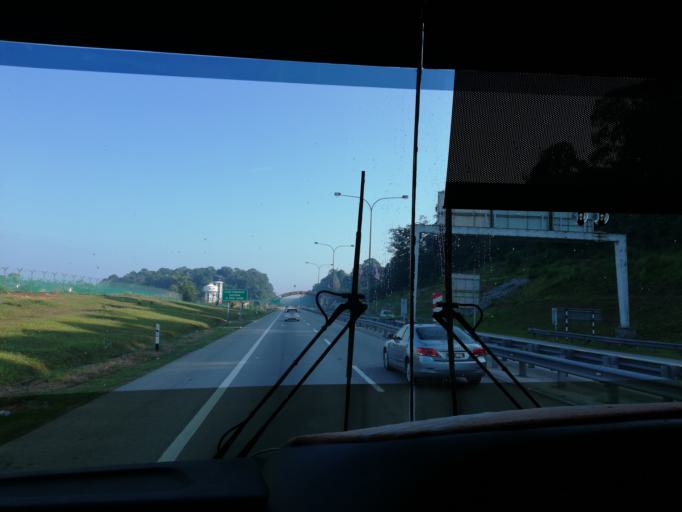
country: MY
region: Negeri Sembilan
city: Port Dickson
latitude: 2.5019
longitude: 101.8654
